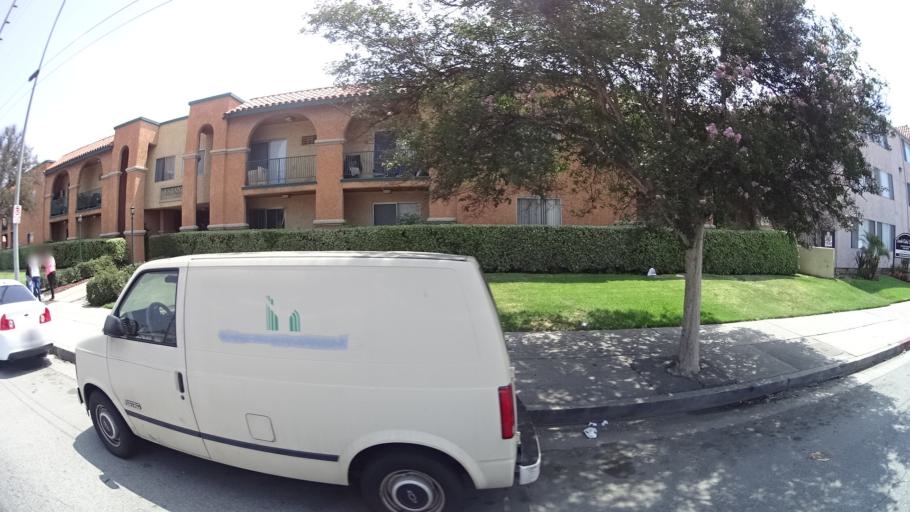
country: US
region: California
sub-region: Los Angeles County
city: Van Nuys
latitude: 34.1913
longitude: -118.4661
